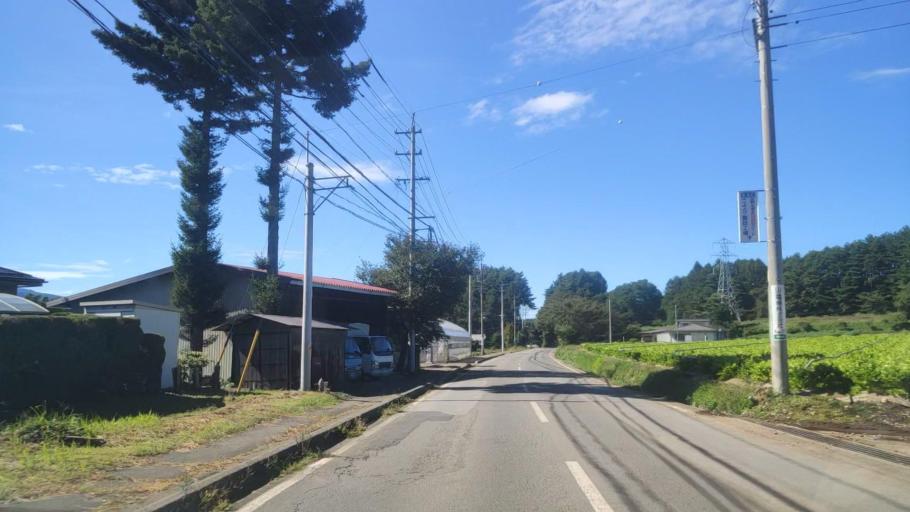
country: JP
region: Nagano
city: Chino
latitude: 35.9488
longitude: 138.2157
